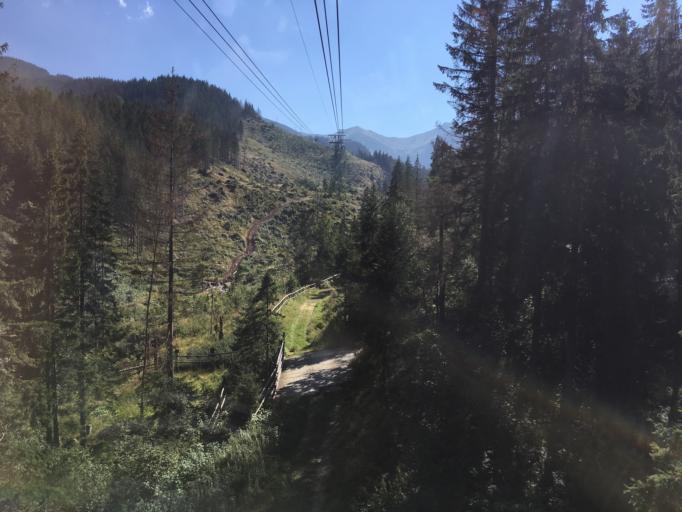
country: PL
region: Lesser Poland Voivodeship
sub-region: Powiat tatrzanski
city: Zakopane
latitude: 49.2678
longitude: 19.9786
